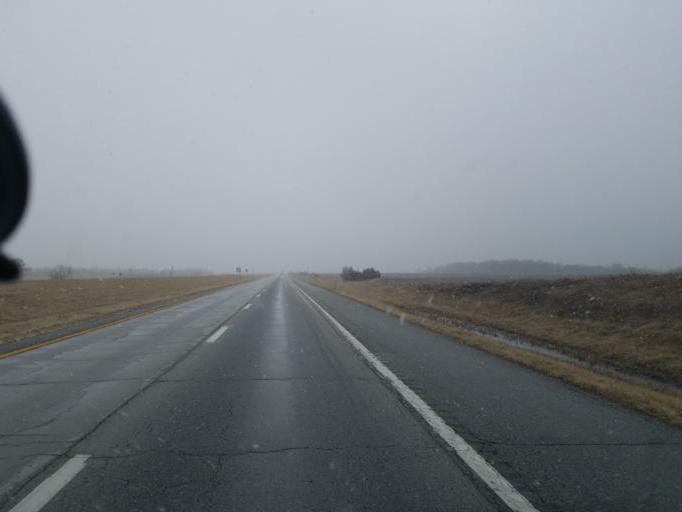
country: US
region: Missouri
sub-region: Macon County
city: La Plata
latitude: 39.9534
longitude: -92.4769
